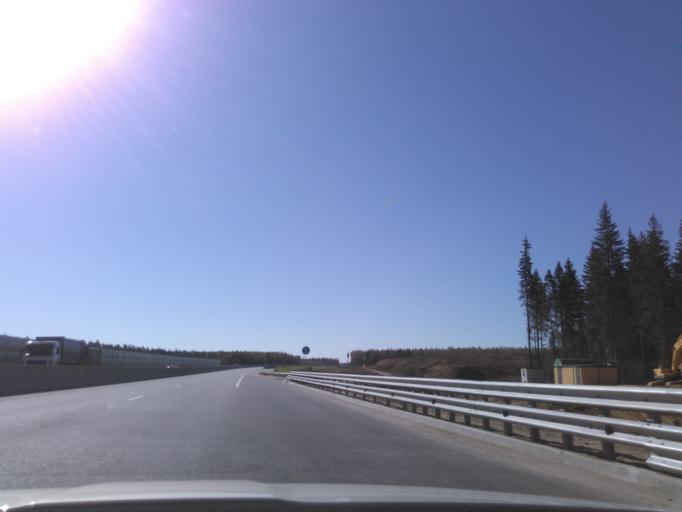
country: RU
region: Moskovskaya
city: Radumlya
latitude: 56.0896
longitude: 37.2003
